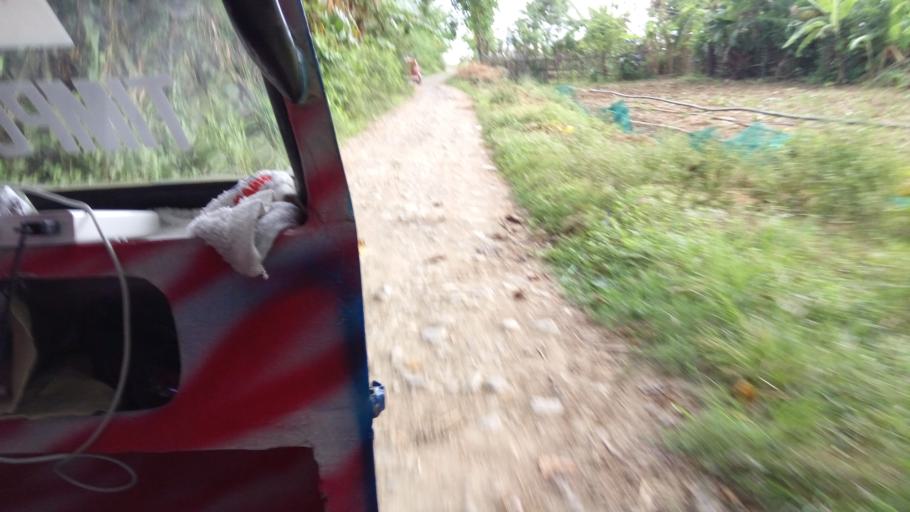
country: PH
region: Ilocos
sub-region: Province of La Union
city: Santo Tomas
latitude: 16.2776
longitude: 120.3872
